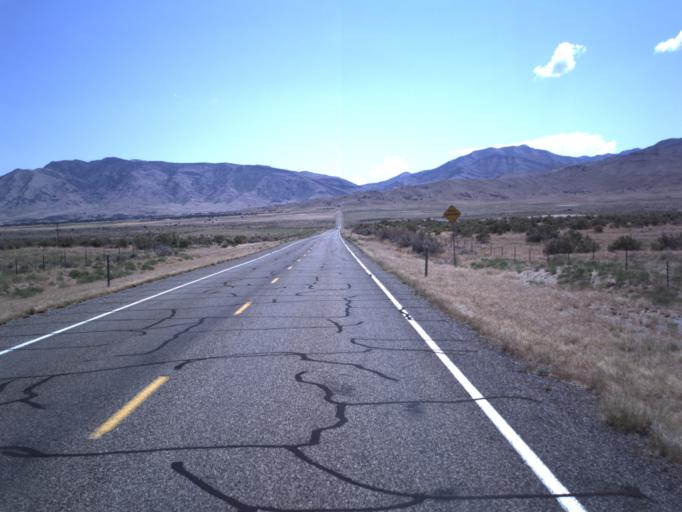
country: US
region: Utah
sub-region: Millard County
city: Delta
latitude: 39.3544
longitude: -112.4147
